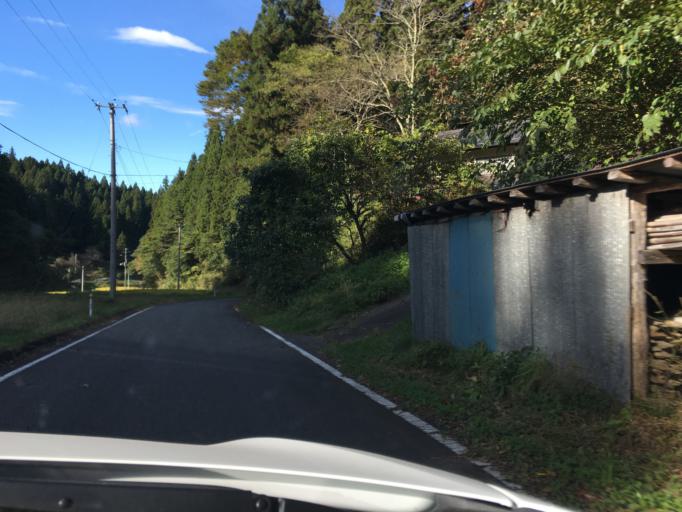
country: JP
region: Fukushima
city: Ishikawa
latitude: 37.1394
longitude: 140.5425
